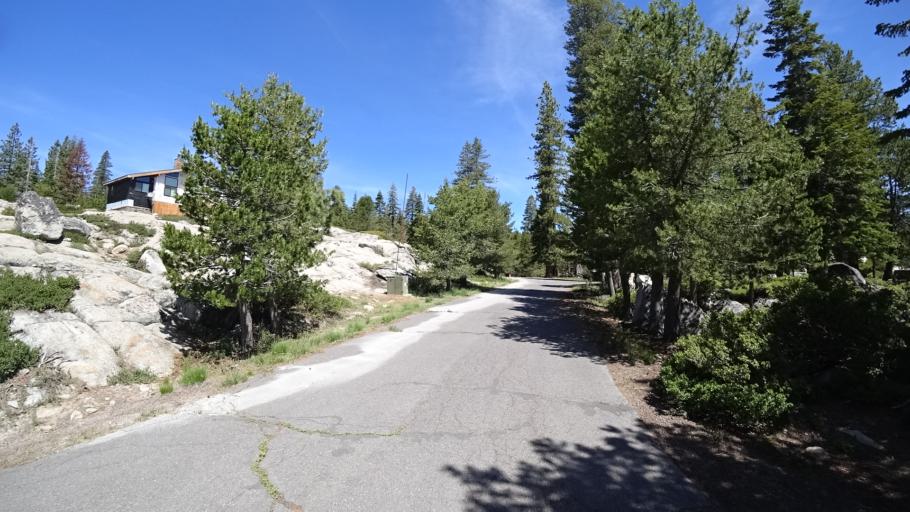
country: US
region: California
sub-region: Calaveras County
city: Arnold
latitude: 38.4389
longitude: -120.0835
